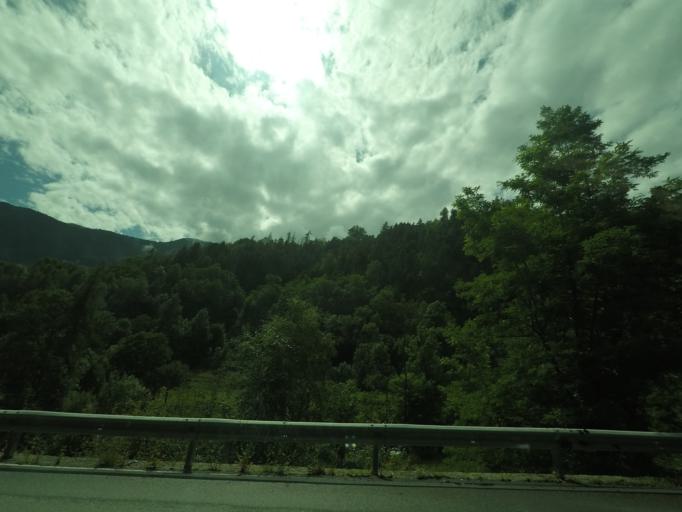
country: IT
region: Aosta Valley
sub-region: Valle d'Aosta
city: Antey-Saint-Andre
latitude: 45.8006
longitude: 7.5903
